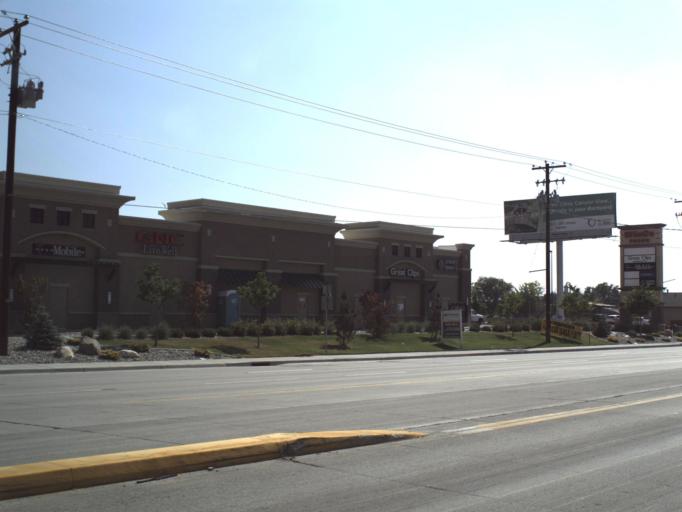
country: US
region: Utah
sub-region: Weber County
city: Ogden
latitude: 41.2444
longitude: -111.9770
